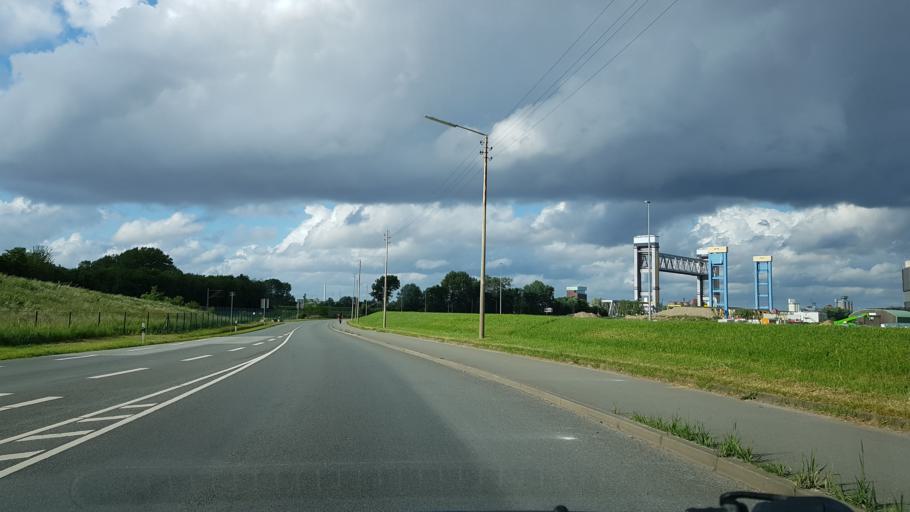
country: DE
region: Hamburg
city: Harburg
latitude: 53.4899
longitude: 9.9443
